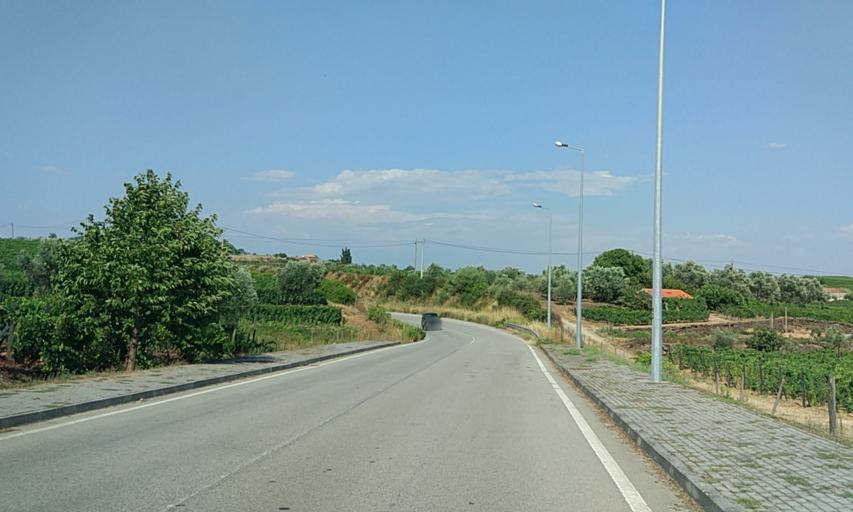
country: PT
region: Vila Real
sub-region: Sabrosa
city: Sabrosa
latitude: 41.2589
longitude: -7.4996
